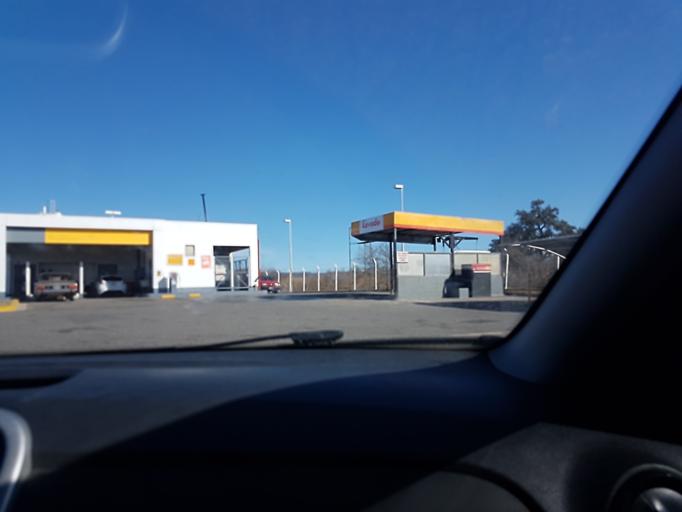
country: AR
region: Cordoba
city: Malagueno
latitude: -31.4374
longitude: -64.3267
